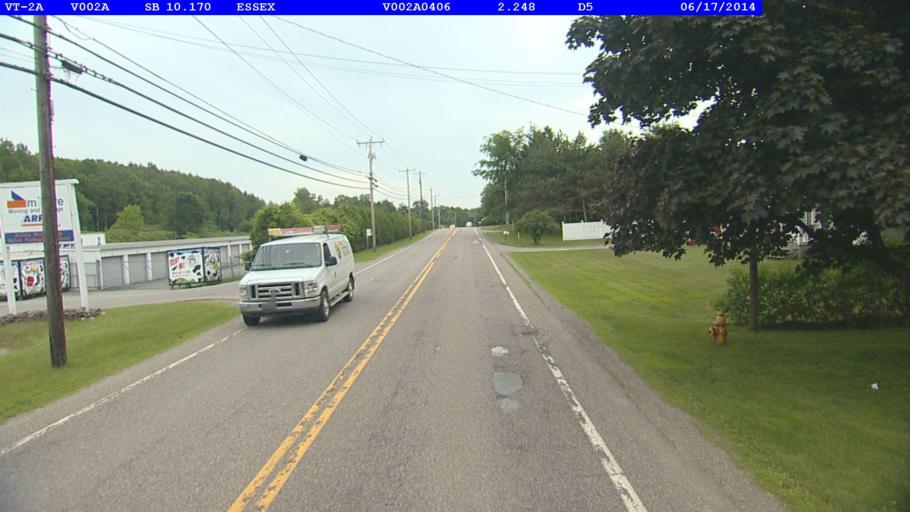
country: US
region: Vermont
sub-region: Chittenden County
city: Essex Junction
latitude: 44.5122
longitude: -73.1203
